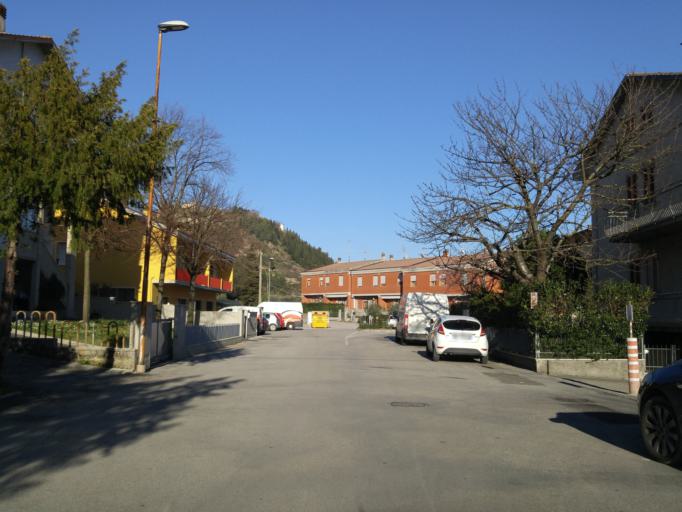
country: IT
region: The Marches
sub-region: Provincia di Pesaro e Urbino
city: Fossombrone
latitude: 43.6860
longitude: 12.7967
